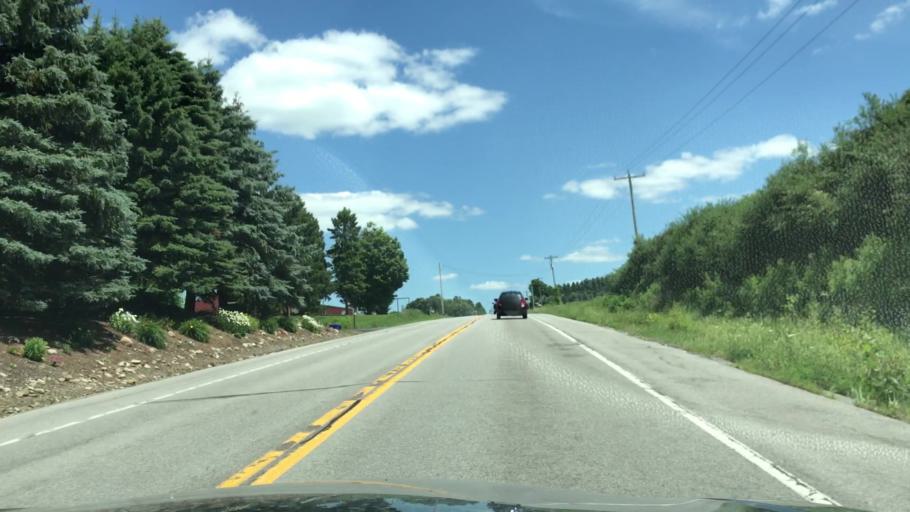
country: US
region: New York
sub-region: Wyoming County
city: Attica
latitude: 42.7557
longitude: -78.2776
